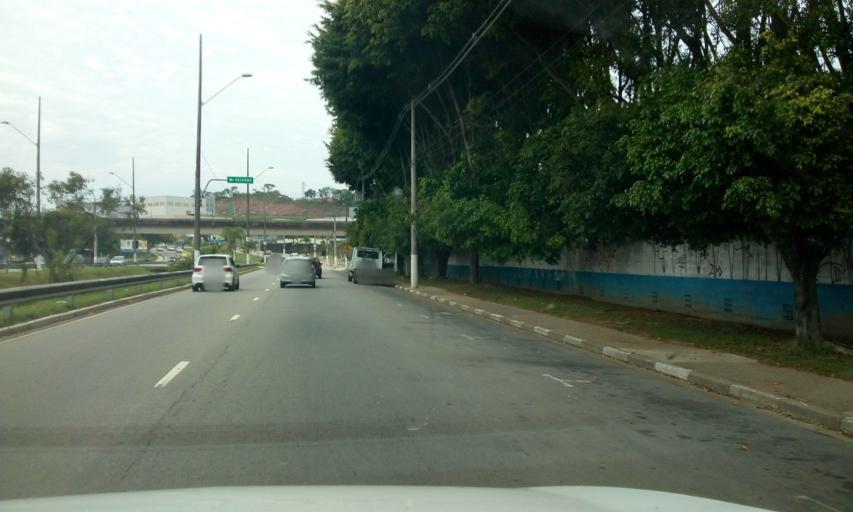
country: BR
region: Sao Paulo
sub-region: Jundiai
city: Jundiai
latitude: -23.2207
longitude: -46.8747
